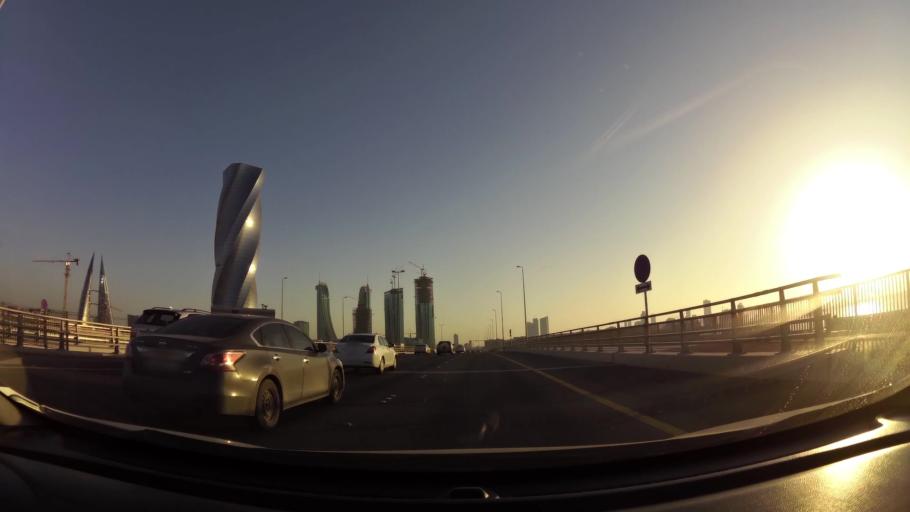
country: BH
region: Muharraq
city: Al Muharraq
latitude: 26.2504
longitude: 50.5771
